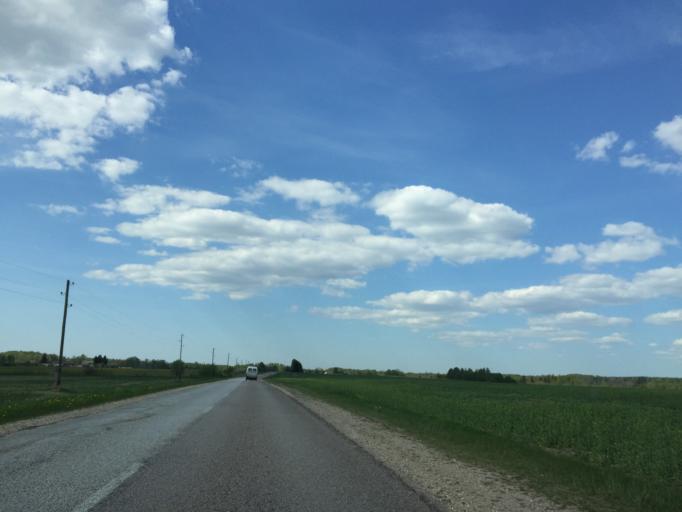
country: LV
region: Limbazu Rajons
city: Limbazi
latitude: 57.4540
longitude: 24.7238
